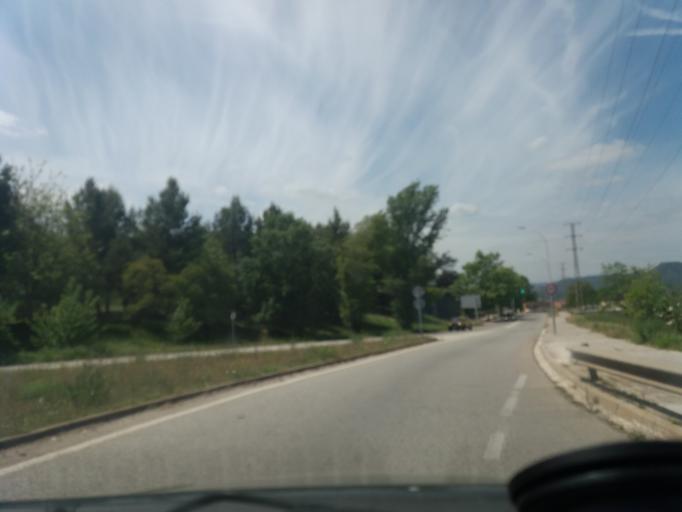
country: ES
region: Catalonia
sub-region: Provincia de Barcelona
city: Manresa
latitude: 41.7213
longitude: 1.8467
